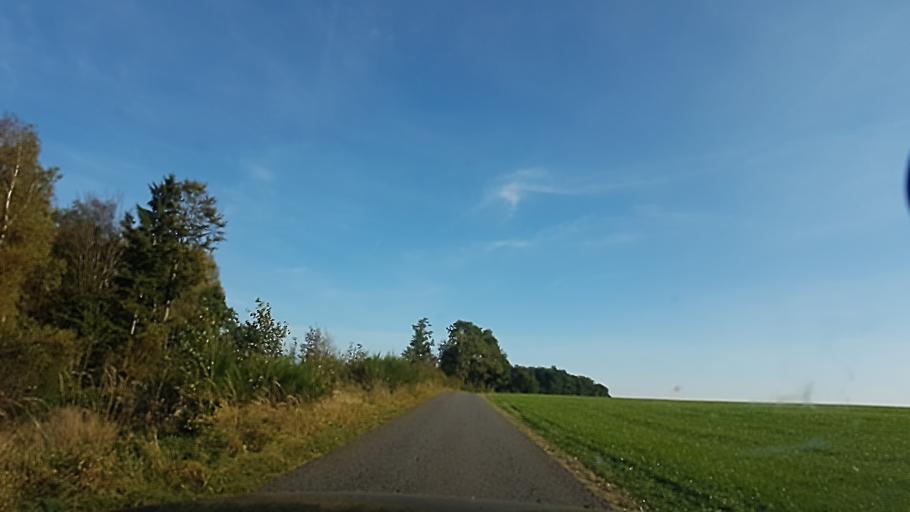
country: DE
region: North Rhine-Westphalia
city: Halver
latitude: 51.1538
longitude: 7.4996
